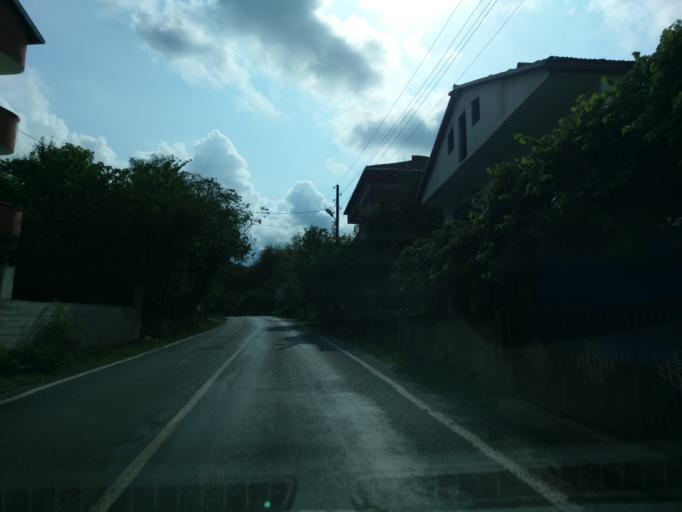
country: TR
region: Sinop
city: Helaldi
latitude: 41.9082
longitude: 34.4396
